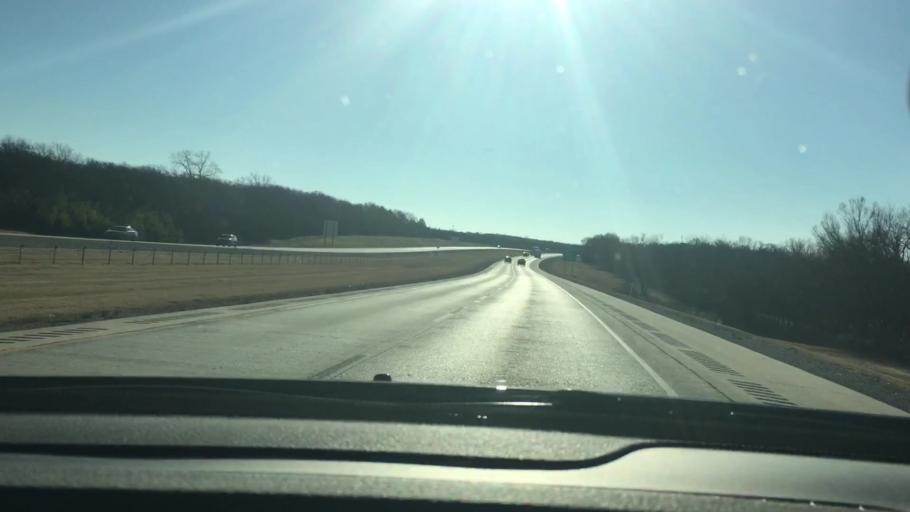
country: US
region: Oklahoma
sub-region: Carter County
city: Ardmore
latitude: 34.1570
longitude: -97.1625
